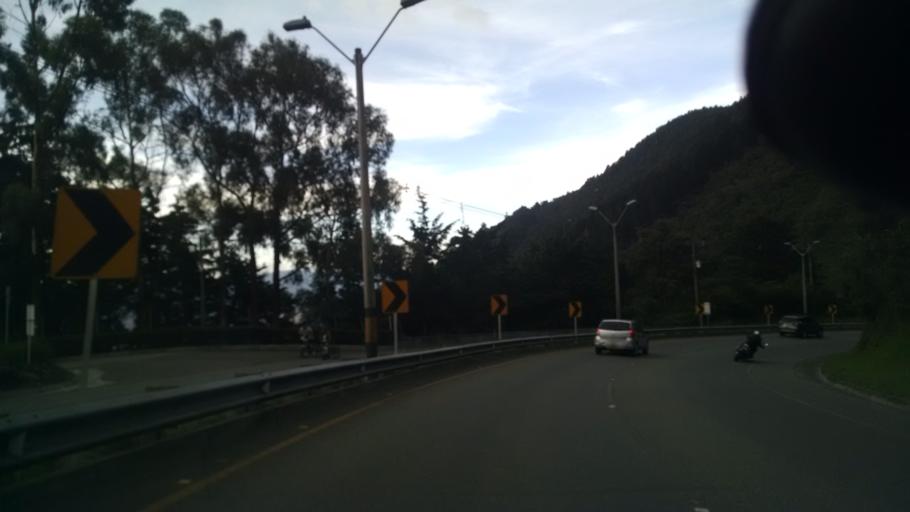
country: CO
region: Antioquia
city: Envigado
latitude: 6.1595
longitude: -75.5467
